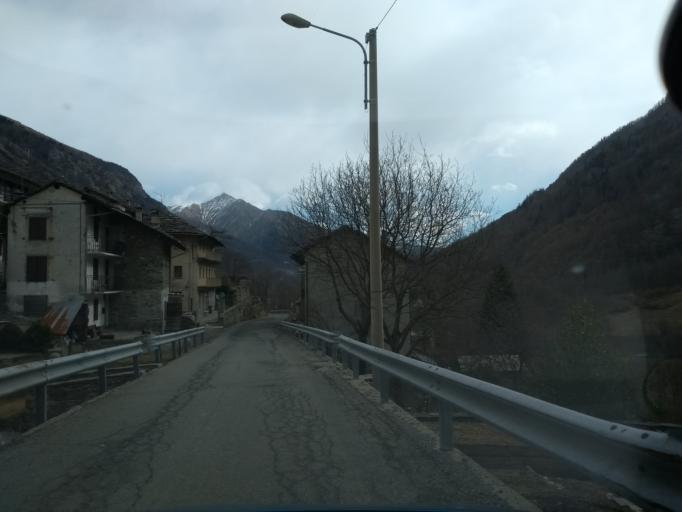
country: IT
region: Piedmont
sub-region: Provincia di Torino
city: Groscavallo
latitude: 45.3690
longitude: 7.2883
